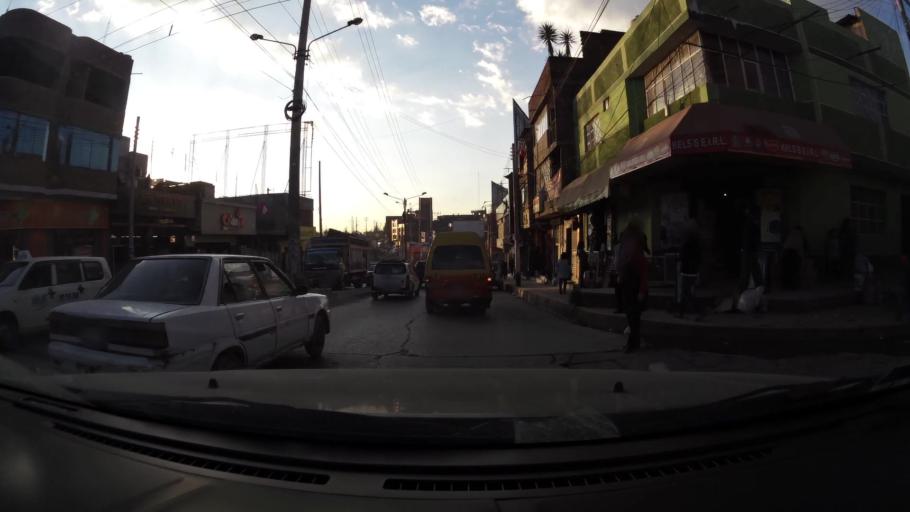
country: PE
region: Junin
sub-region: Provincia de Huancayo
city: El Tambo
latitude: -12.0540
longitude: -75.2249
